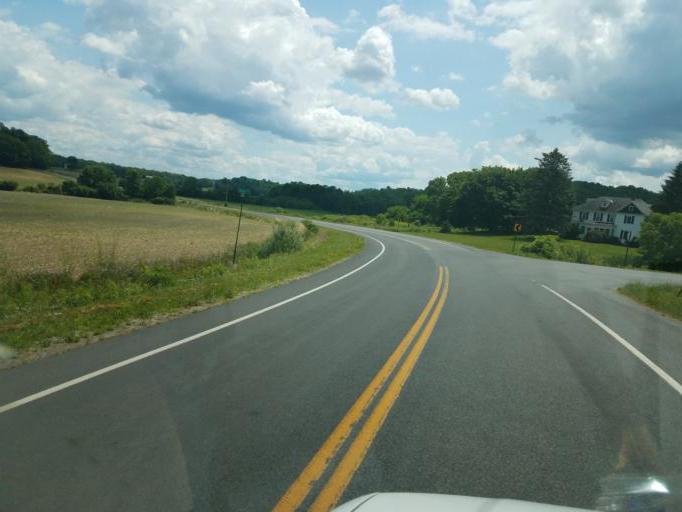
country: US
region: New York
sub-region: Wayne County
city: Clyde
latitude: 43.0614
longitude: -76.8566
